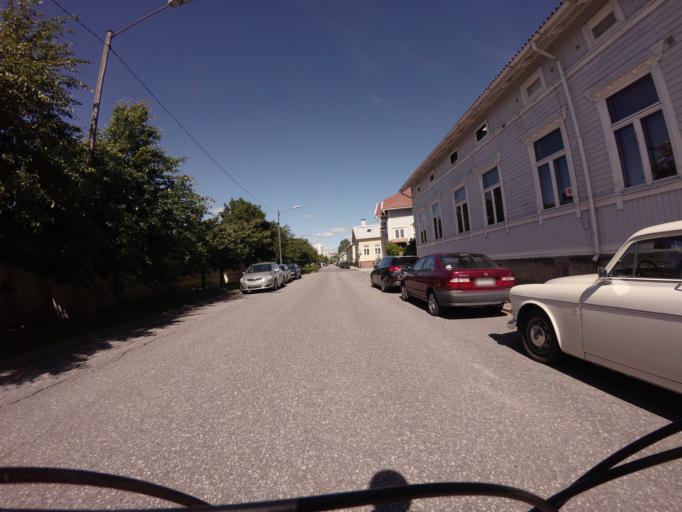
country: FI
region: Varsinais-Suomi
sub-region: Turku
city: Turku
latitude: 60.4487
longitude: 22.2423
